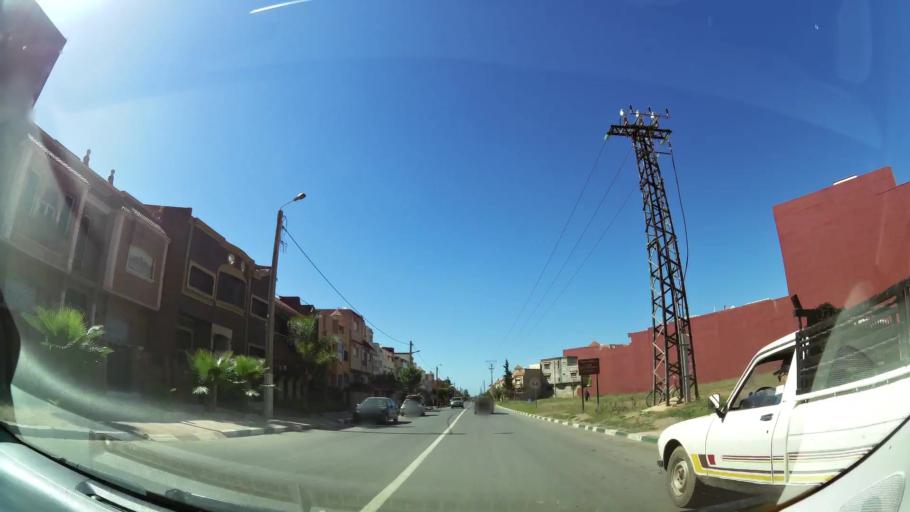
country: MA
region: Oriental
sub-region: Berkane-Taourirt
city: Berkane
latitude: 34.9362
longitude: -2.3236
